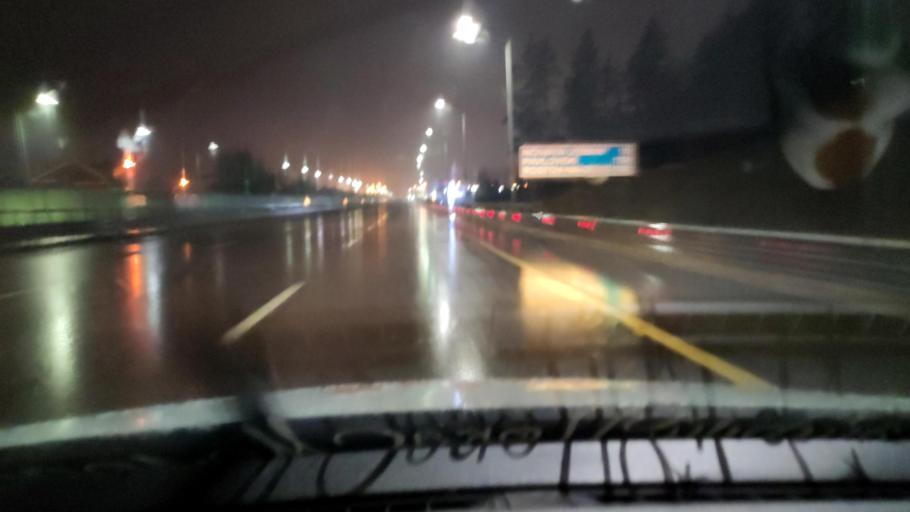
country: RU
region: Voronezj
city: Somovo
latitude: 51.6888
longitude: 39.3026
